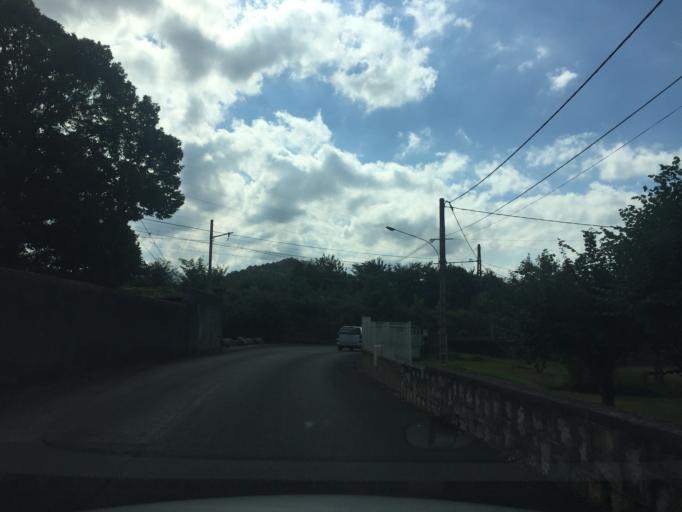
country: FR
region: Midi-Pyrenees
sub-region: Departement de la Haute-Garonne
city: Gourdan-Polignan
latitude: 43.0769
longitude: 0.5813
